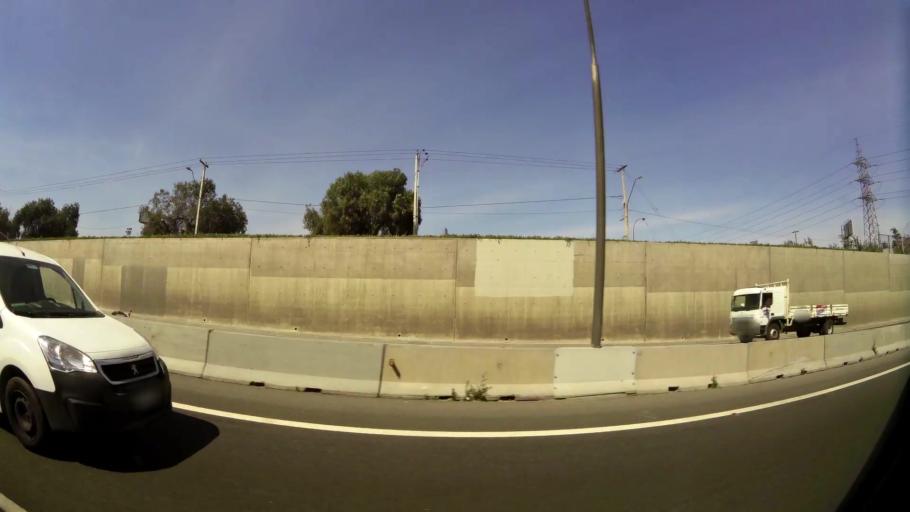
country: CL
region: Santiago Metropolitan
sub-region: Provincia de Santiago
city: Santiago
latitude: -33.5206
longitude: -70.6758
